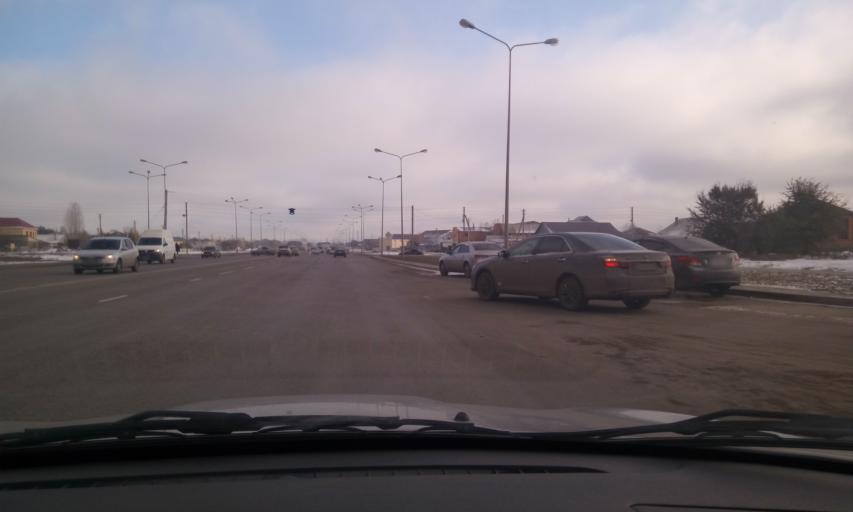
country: KZ
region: Astana Qalasy
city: Astana
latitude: 51.1309
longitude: 71.5041
